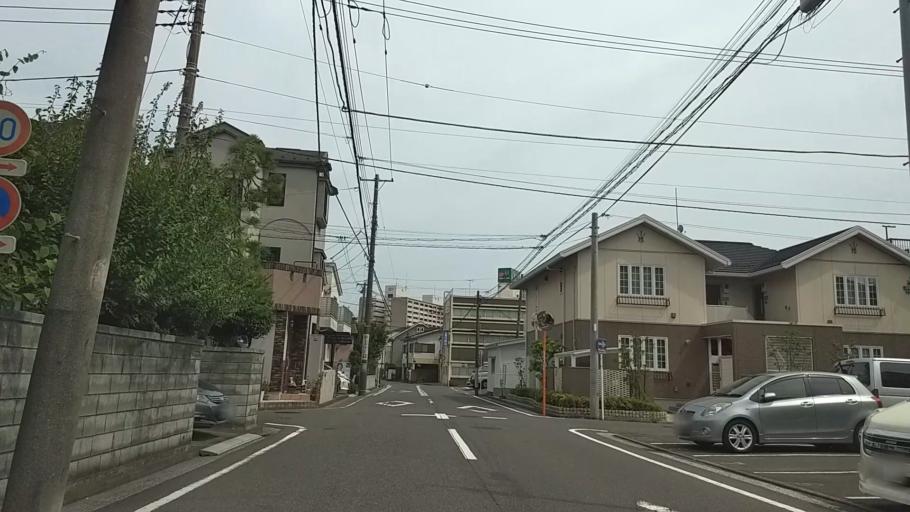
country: JP
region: Kanagawa
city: Yokohama
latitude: 35.4366
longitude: 139.6002
